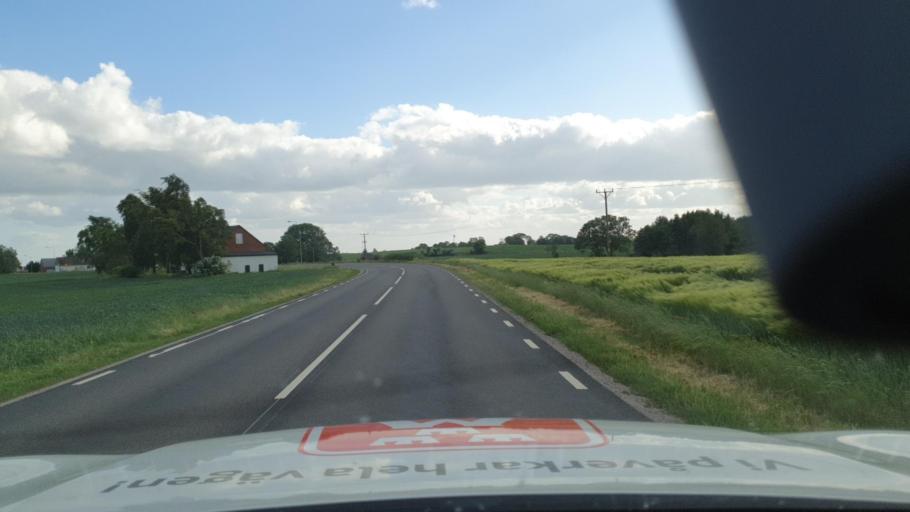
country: SE
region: Skane
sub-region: Tomelilla Kommun
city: Tomelilla
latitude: 55.5869
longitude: 14.0179
